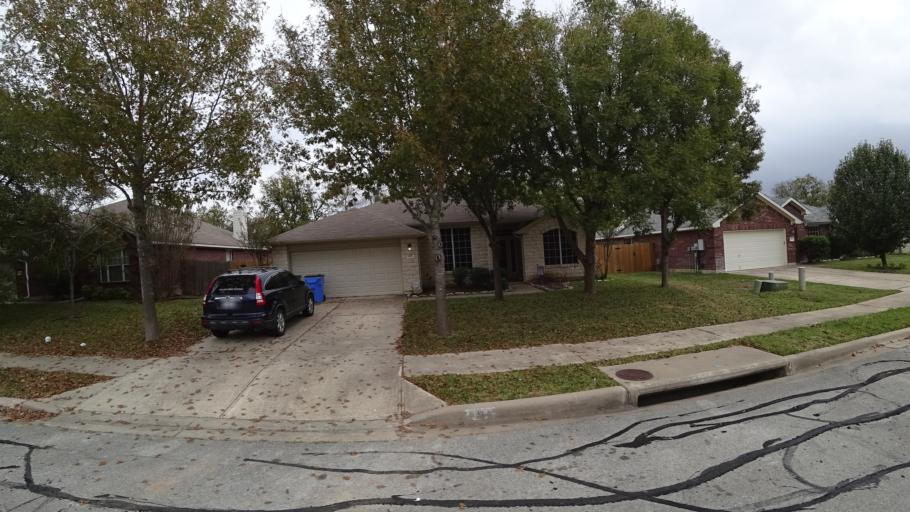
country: US
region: Texas
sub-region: Travis County
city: Pflugerville
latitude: 30.4335
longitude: -97.6052
